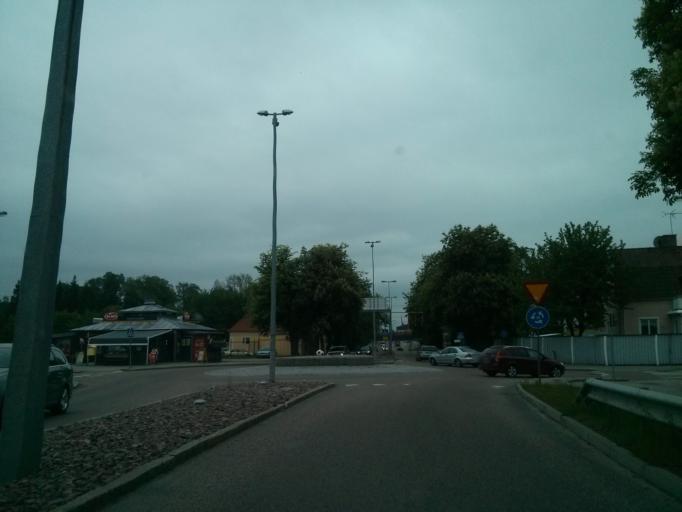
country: SE
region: Soedermanland
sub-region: Nykopings Kommun
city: Nykoping
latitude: 58.7586
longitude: 16.9992
